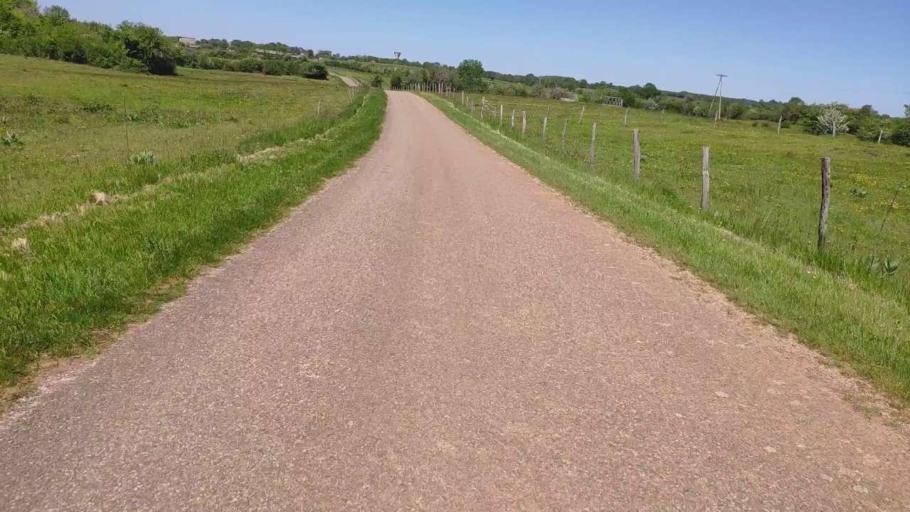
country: FR
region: Franche-Comte
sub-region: Departement du Jura
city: Poligny
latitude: 46.7351
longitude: 5.7185
